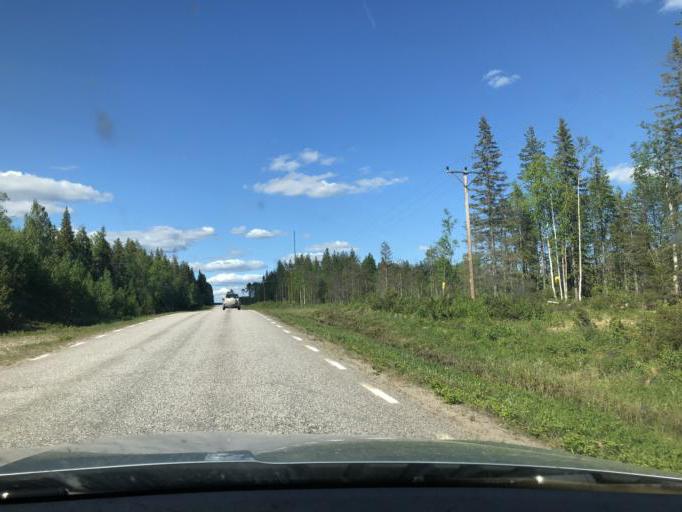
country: SE
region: Norrbotten
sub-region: Kalix Kommun
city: Kalix
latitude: 66.0356
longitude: 23.1722
